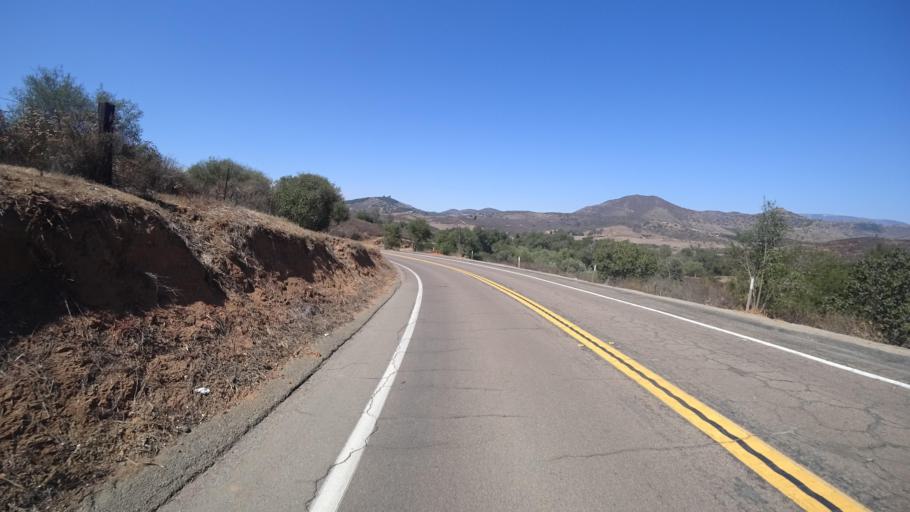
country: US
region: California
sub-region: San Diego County
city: Hidden Meadows
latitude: 33.2833
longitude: -117.0837
